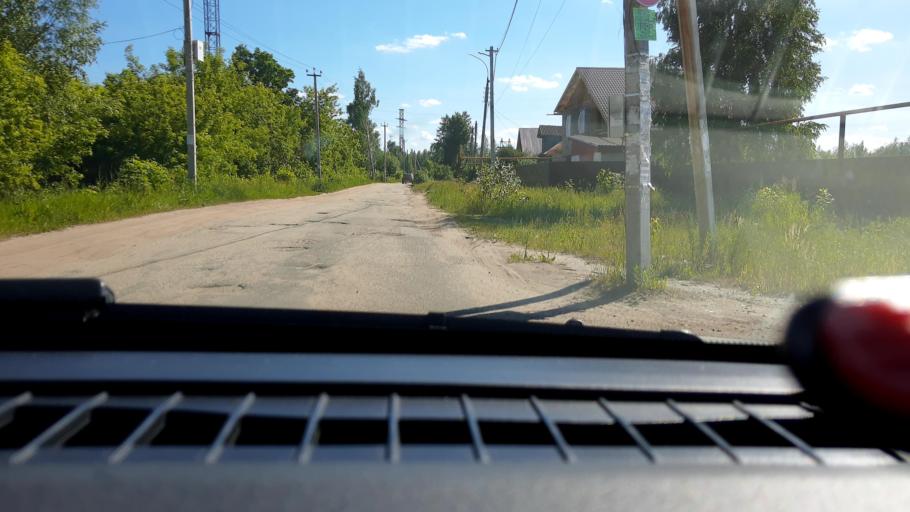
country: RU
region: Nizjnij Novgorod
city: Gidrotorf
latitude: 56.5188
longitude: 43.5401
